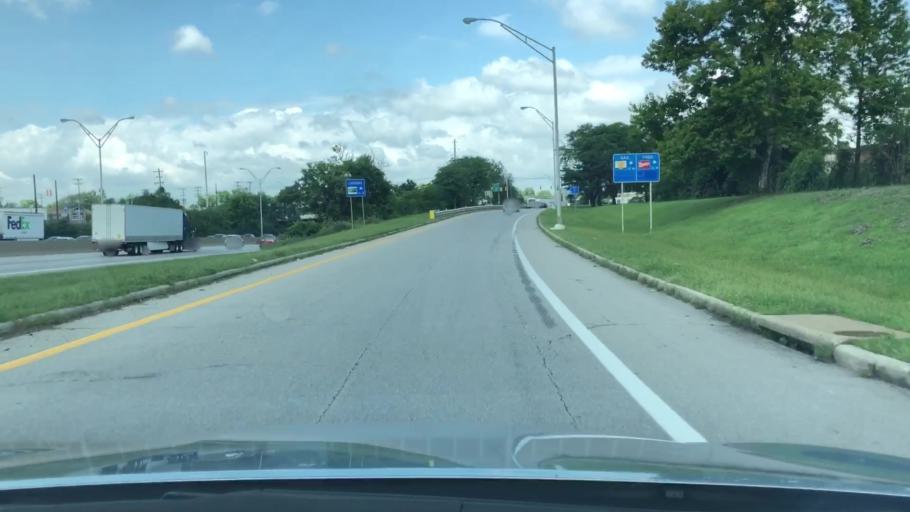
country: US
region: Ohio
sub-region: Franklin County
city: Columbus
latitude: 40.0132
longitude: -82.9925
